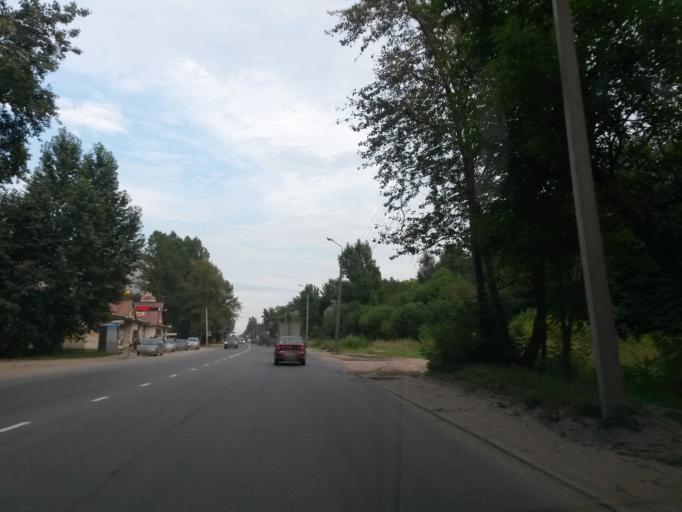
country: RU
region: Jaroslavl
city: Yaroslavl
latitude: 57.5836
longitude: 39.8244
